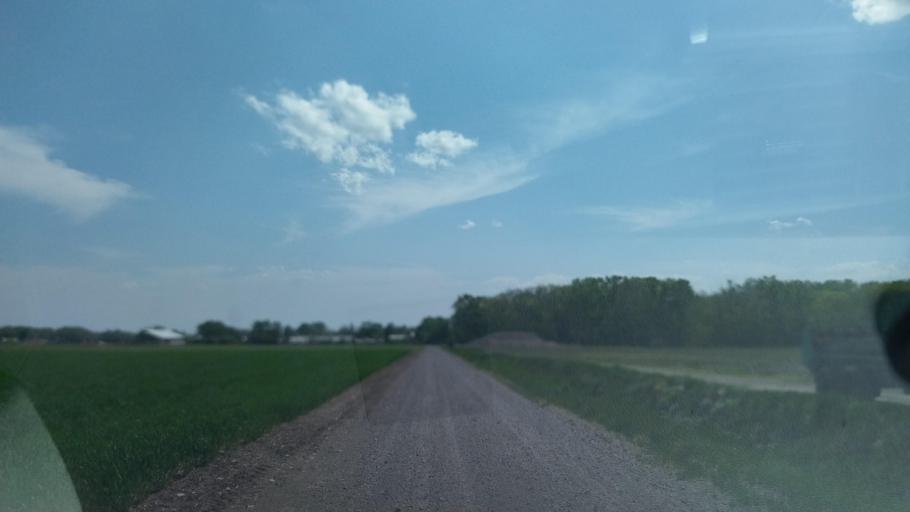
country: JP
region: Hokkaido
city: Otofuke
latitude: 43.1365
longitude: 143.2193
